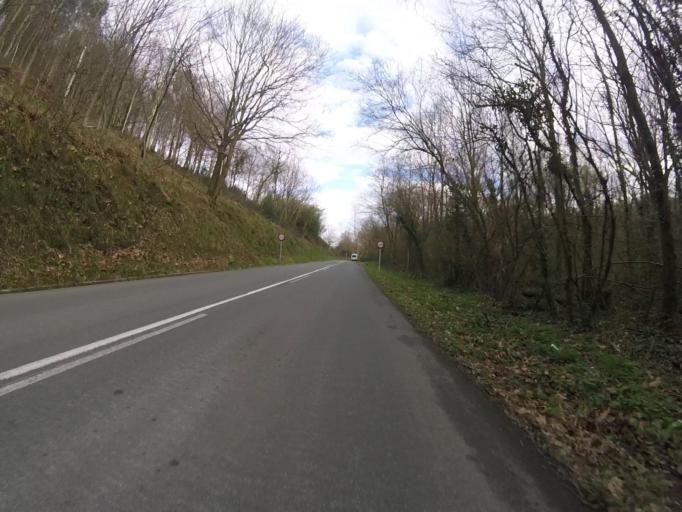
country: ES
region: Basque Country
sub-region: Provincia de Guipuzcoa
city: Irun
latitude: 43.3206
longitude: -1.8218
